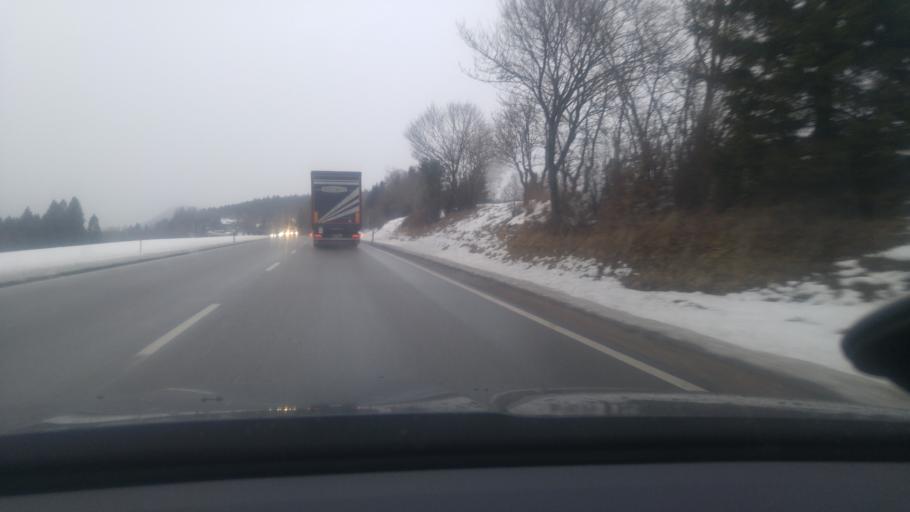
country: DE
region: Baden-Wuerttemberg
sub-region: Freiburg Region
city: Hinterzarten
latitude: 47.9096
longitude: 8.1158
